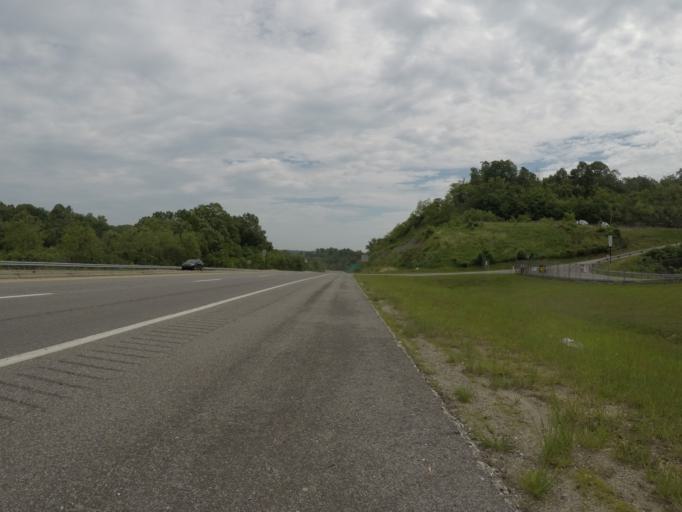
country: US
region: West Virginia
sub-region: Wayne County
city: Kenova
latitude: 38.3816
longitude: -82.5803
